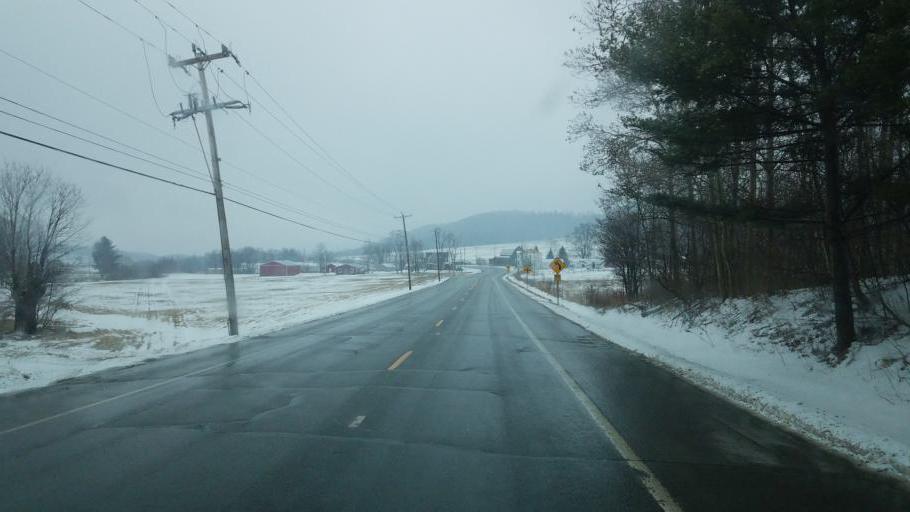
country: US
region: New York
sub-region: Steuben County
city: Canisteo
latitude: 42.1158
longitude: -77.4945
